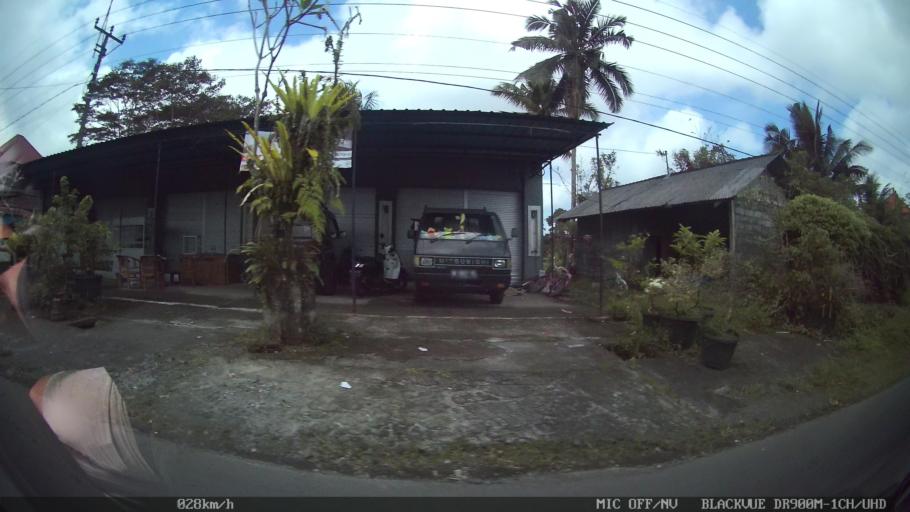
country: ID
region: Bali
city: Banjar Abuan
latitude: -8.4587
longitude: 115.3400
